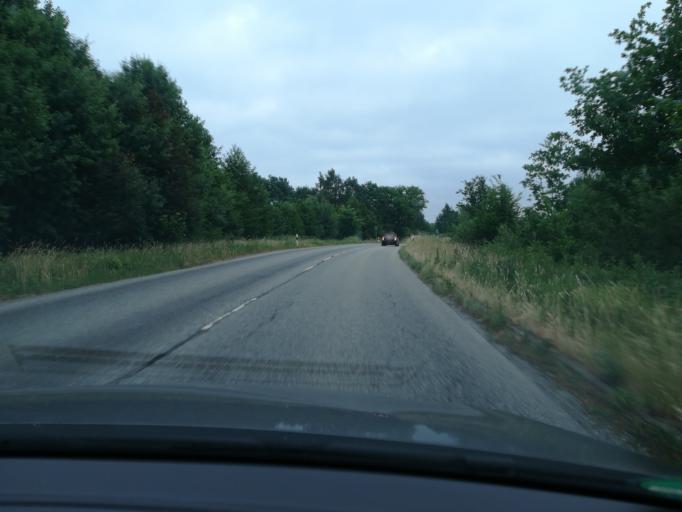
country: DE
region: Schleswig-Holstein
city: Siek
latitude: 53.6421
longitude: 10.3030
